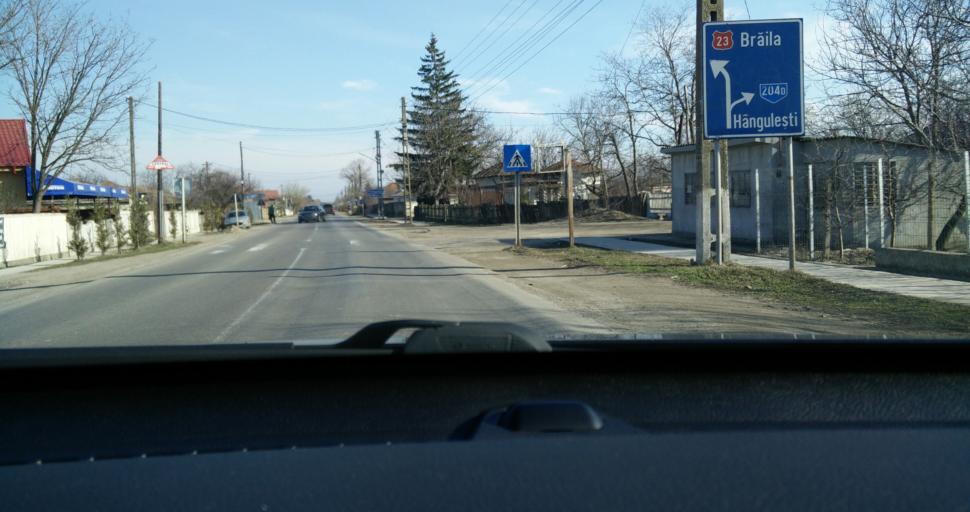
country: RO
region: Vrancea
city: Vulturu de Sus
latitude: 45.6175
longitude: 27.4244
